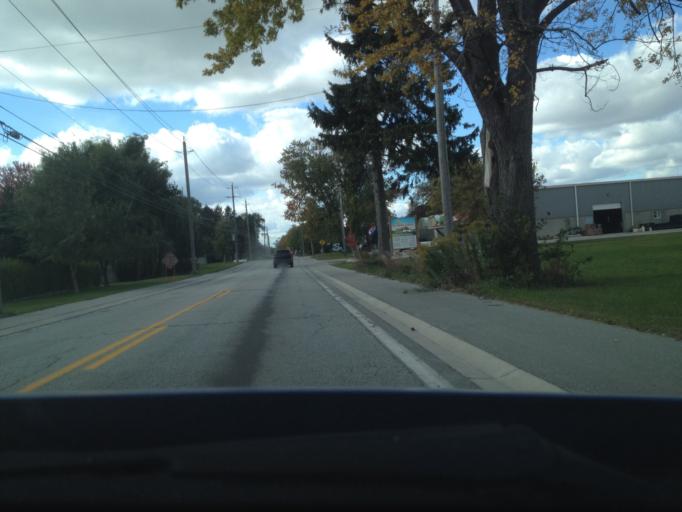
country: CA
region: Ontario
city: Amherstburg
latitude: 42.0392
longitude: -82.6478
